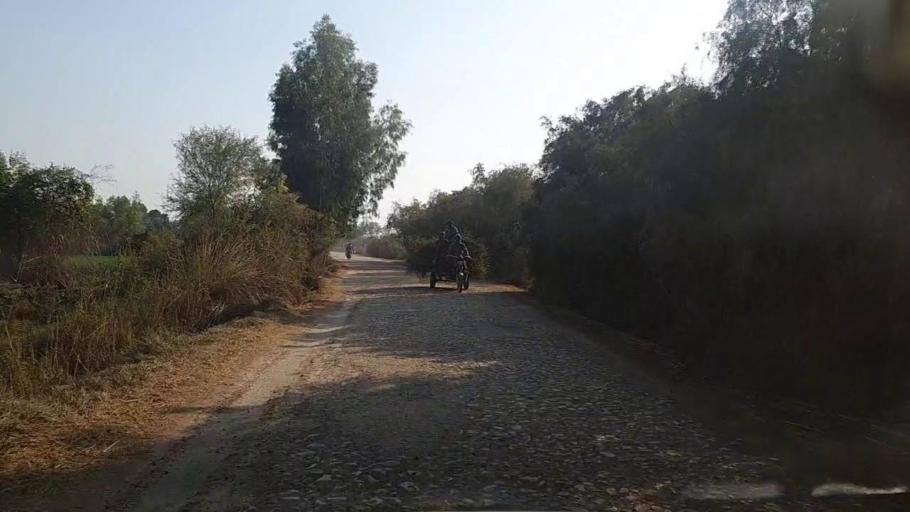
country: PK
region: Sindh
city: Mirpur Mathelo
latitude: 27.8854
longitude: 69.6109
